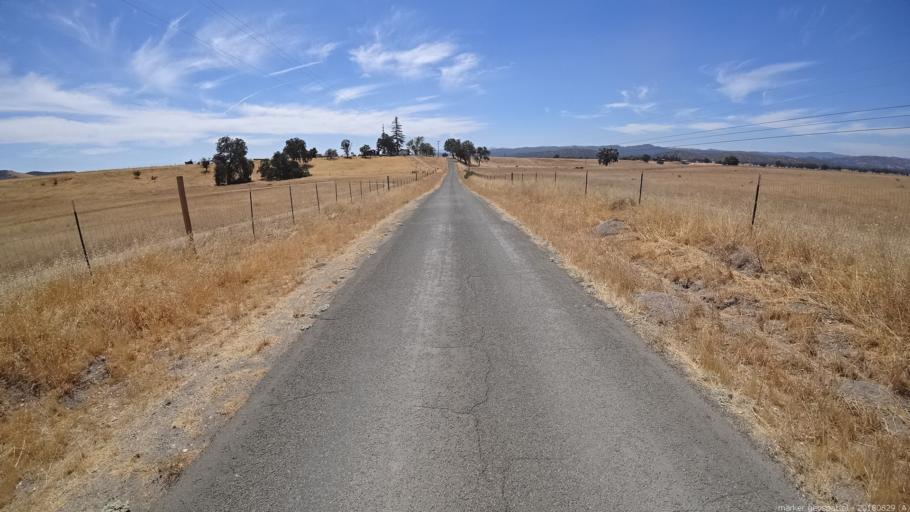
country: US
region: California
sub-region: Monterey County
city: King City
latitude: 35.9490
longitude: -121.0642
